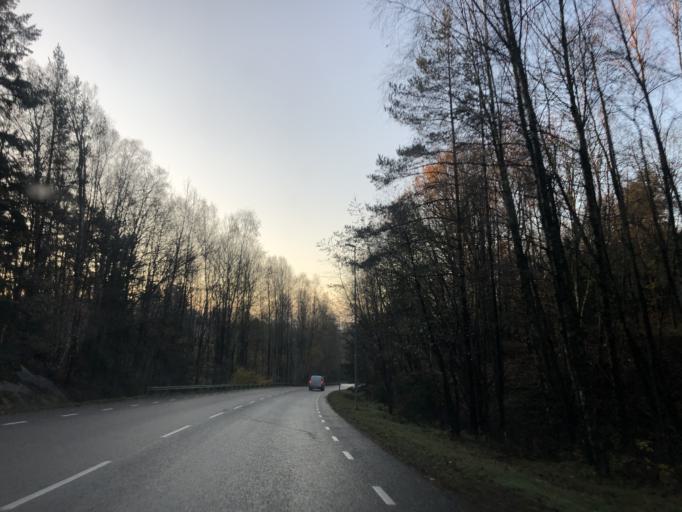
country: SE
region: Vaestra Goetaland
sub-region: Goteborg
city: Gardsten
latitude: 57.7936
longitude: 12.0310
